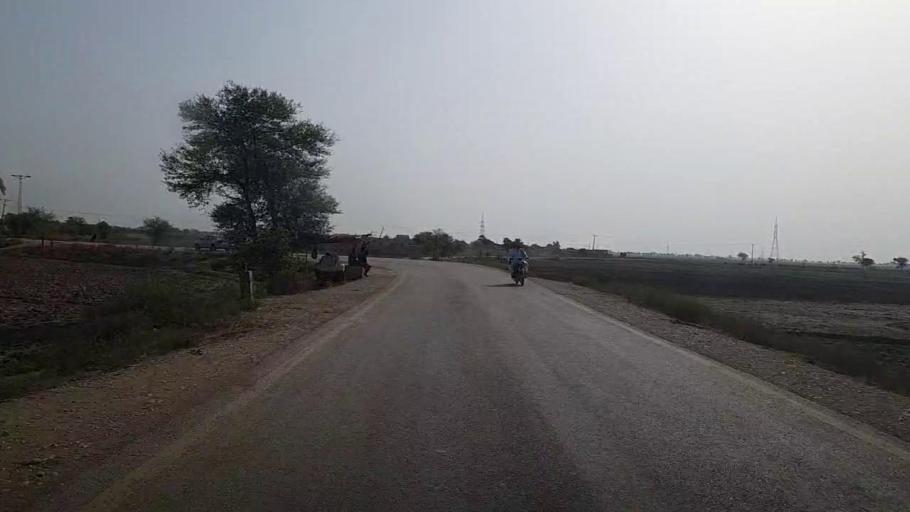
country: PK
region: Sindh
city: Khairpur Nathan Shah
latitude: 27.0989
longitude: 67.7549
